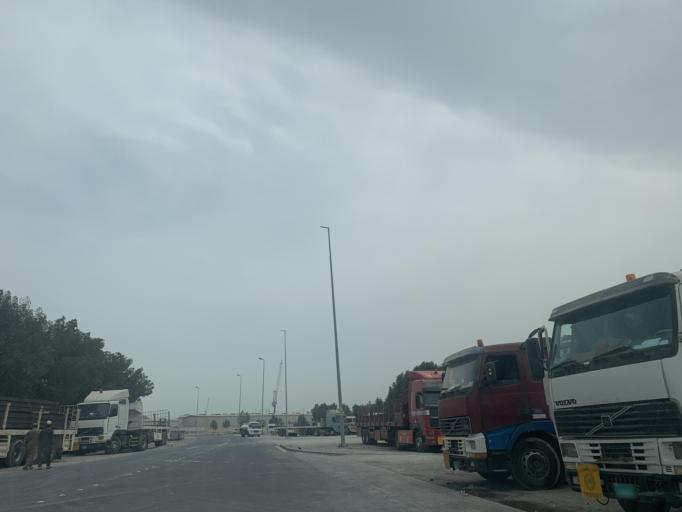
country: BH
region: Muharraq
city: Al Hadd
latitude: 26.2111
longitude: 50.6673
